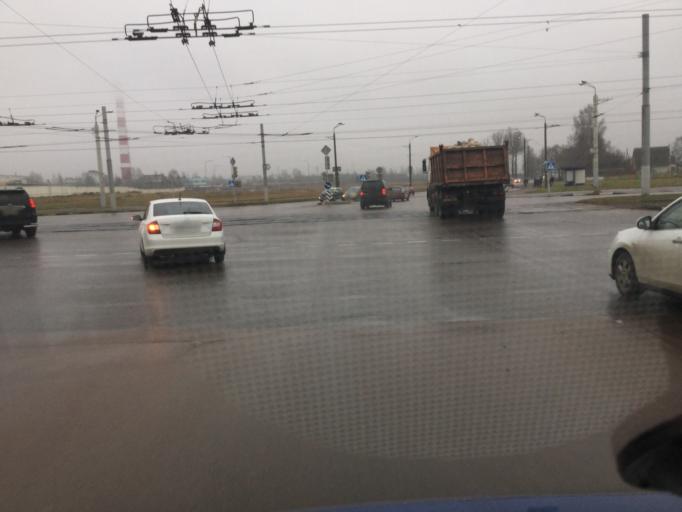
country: BY
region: Vitebsk
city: Vitebsk
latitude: 55.1579
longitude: 30.2329
